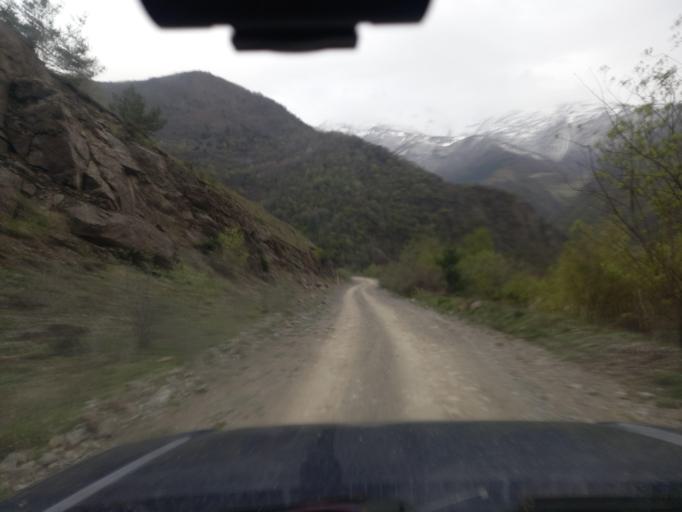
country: RU
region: North Ossetia
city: Mizur
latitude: 42.8511
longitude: 44.1639
